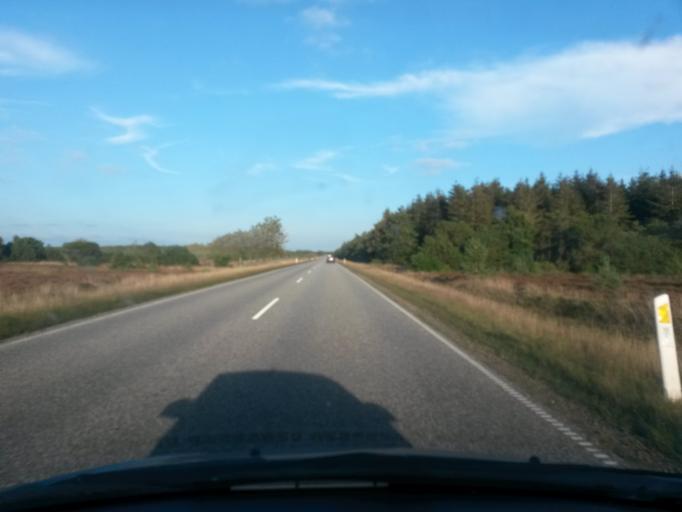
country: DK
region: Central Jutland
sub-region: Herning Kommune
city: Sunds
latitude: 56.3346
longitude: 9.0347
